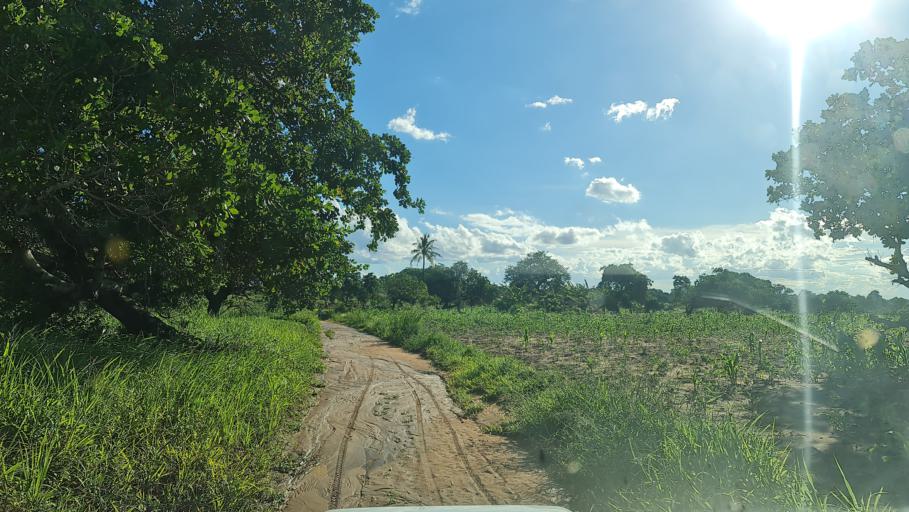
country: MZ
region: Nampula
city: Ilha de Mocambique
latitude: -14.9320
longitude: 40.2148
